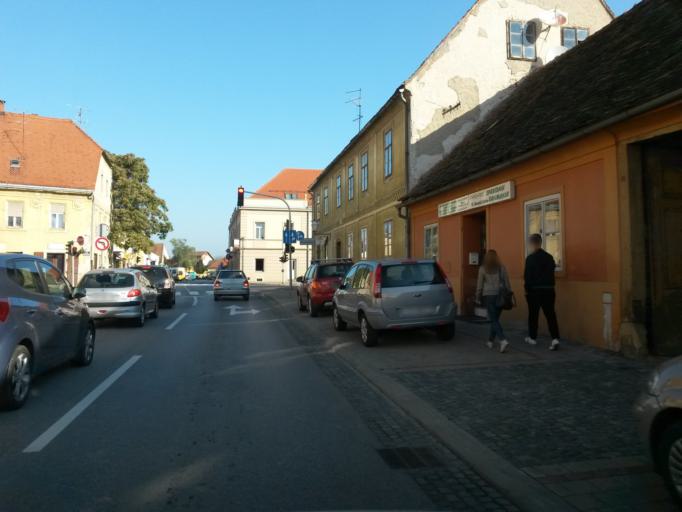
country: HR
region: Varazdinska
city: Varazdin
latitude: 46.3093
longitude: 16.3404
